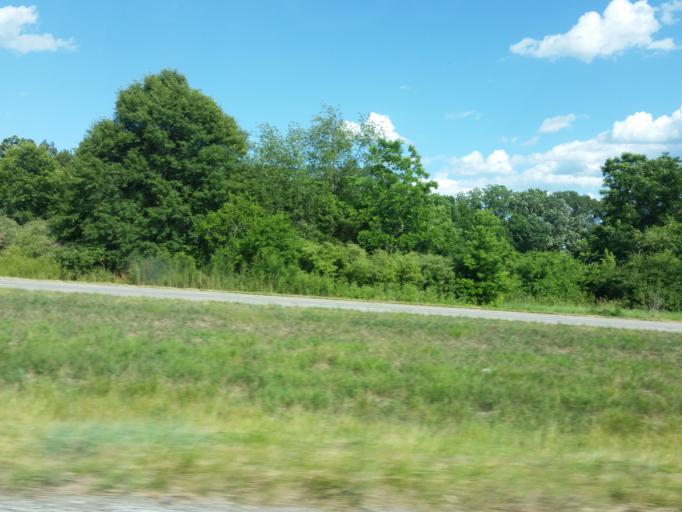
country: US
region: Missouri
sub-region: Lewis County
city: Canton
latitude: 40.1531
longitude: -91.5372
